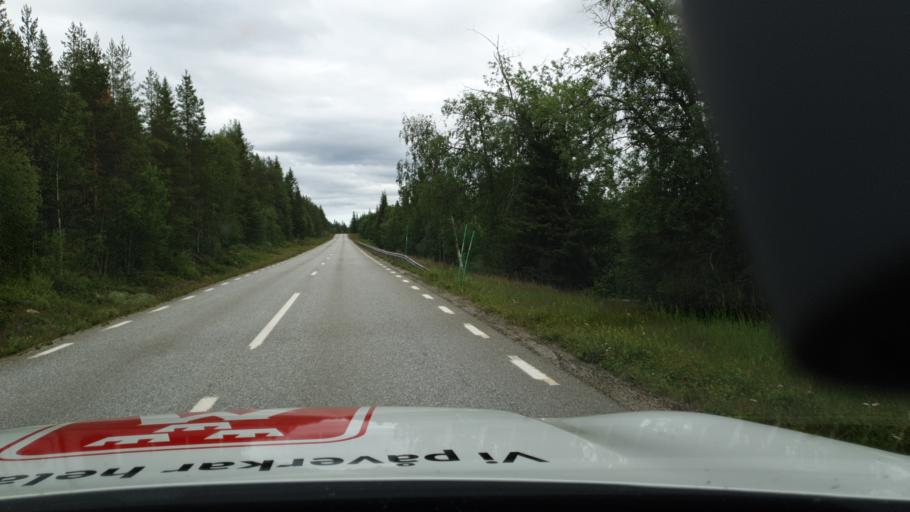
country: SE
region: Vaesterbotten
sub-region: Lycksele Kommun
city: Soderfors
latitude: 64.6853
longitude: 17.8001
